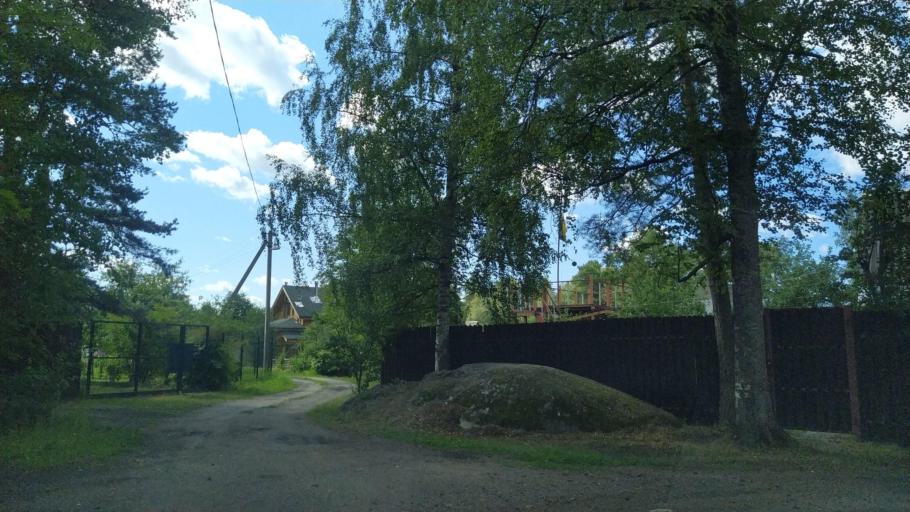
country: RU
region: Leningrad
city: Priozersk
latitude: 61.0019
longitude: 30.1711
